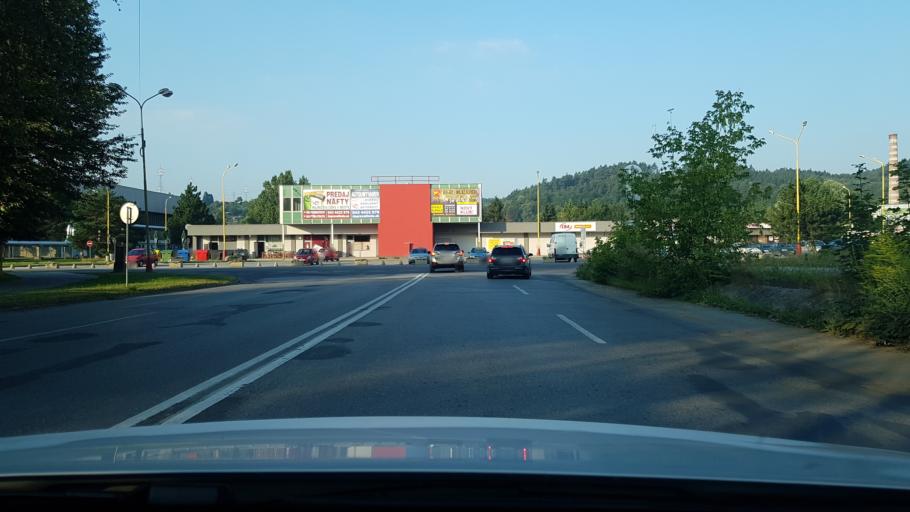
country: SK
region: Trenciansky
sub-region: Okres Povazska Bystrica
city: Povazska Bystrica
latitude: 49.1202
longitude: 18.4258
